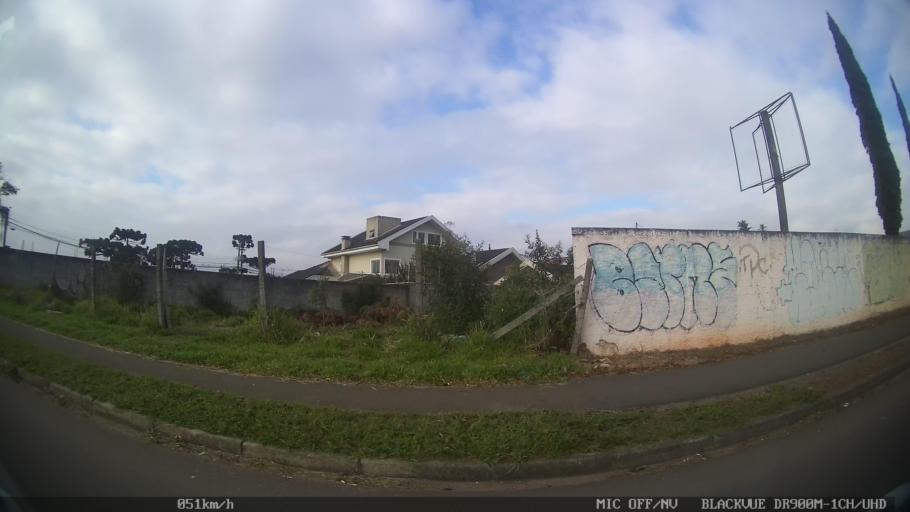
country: BR
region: Parana
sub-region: Almirante Tamandare
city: Almirante Tamandare
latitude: -25.3934
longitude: -49.3402
